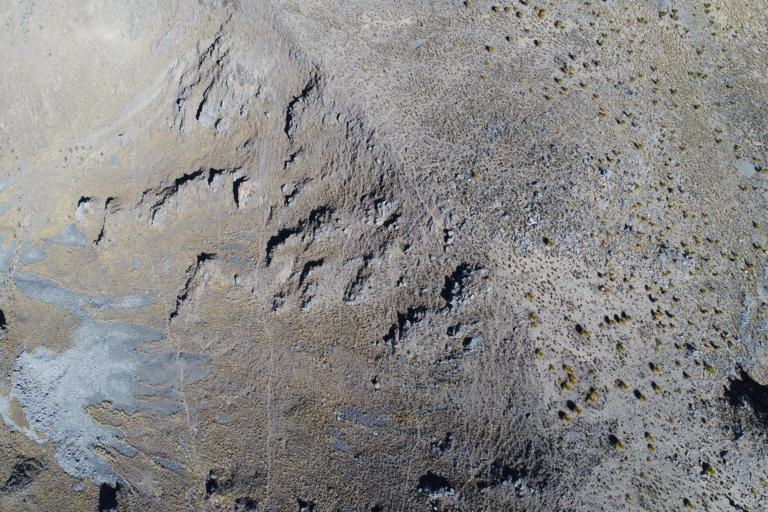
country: BO
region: La Paz
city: Viloco
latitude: -16.8117
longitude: -67.5447
